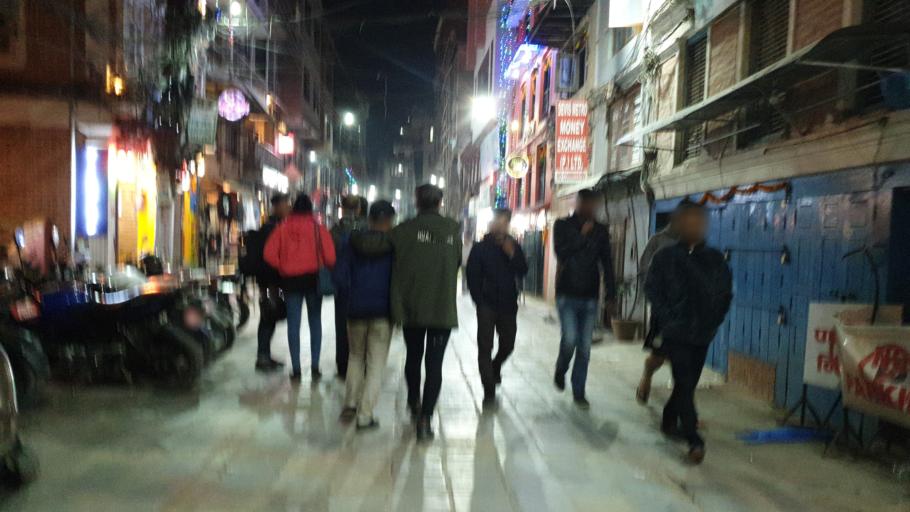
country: NP
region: Central Region
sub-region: Bagmati Zone
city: Kathmandu
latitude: 27.7034
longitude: 85.3076
